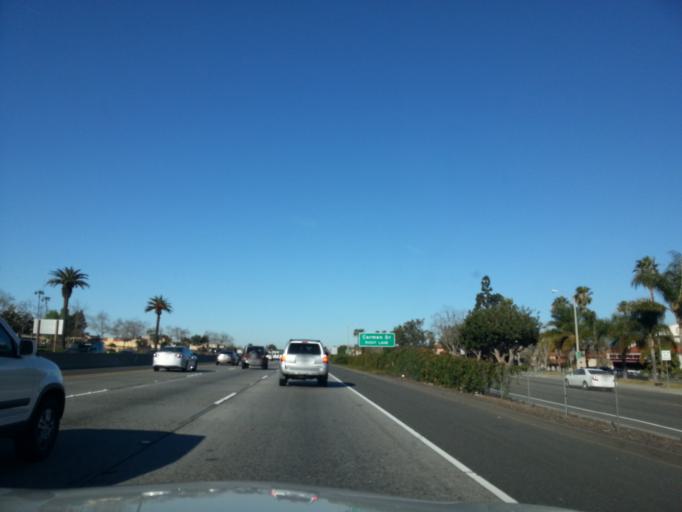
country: US
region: California
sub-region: Ventura County
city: Camarillo
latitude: 34.2176
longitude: -119.0430
